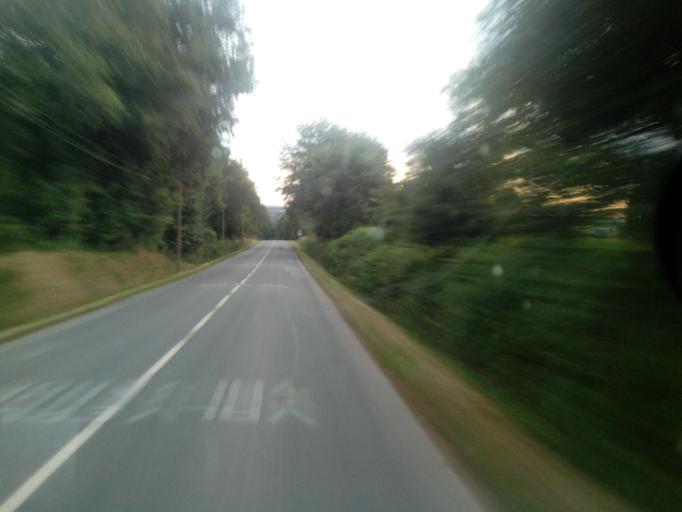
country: FR
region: Brittany
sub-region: Departement du Morbihan
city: Plumelec
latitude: 47.8296
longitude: -2.6500
